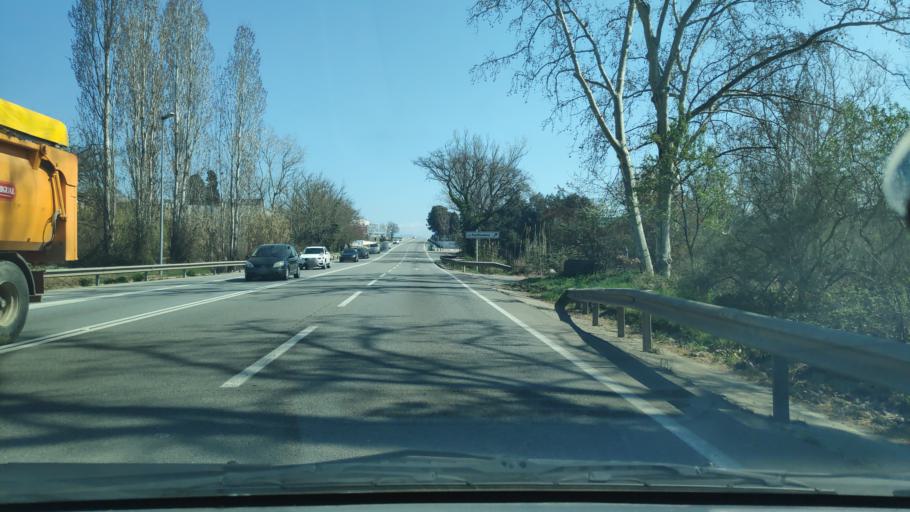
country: ES
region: Catalonia
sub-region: Provincia de Barcelona
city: Polinya
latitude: 41.5334
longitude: 2.1561
